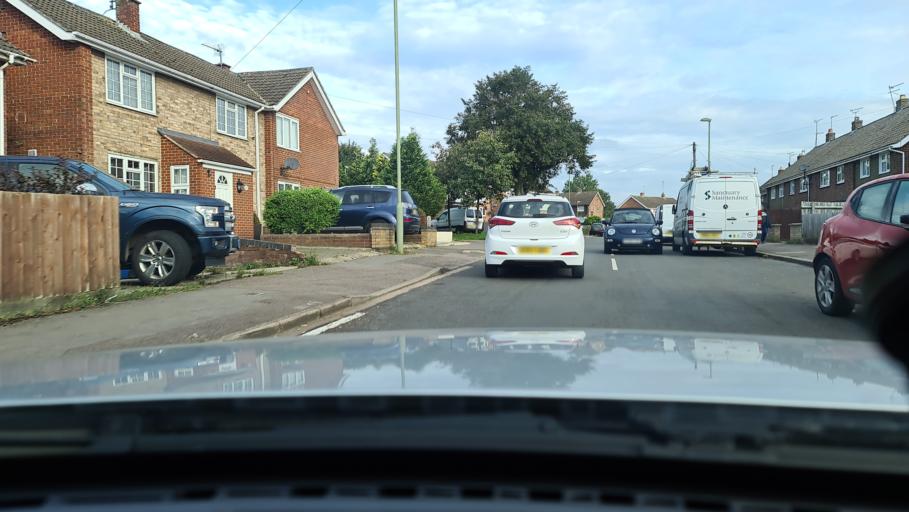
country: GB
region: England
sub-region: Oxfordshire
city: Banbury
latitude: 52.0647
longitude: -1.3648
